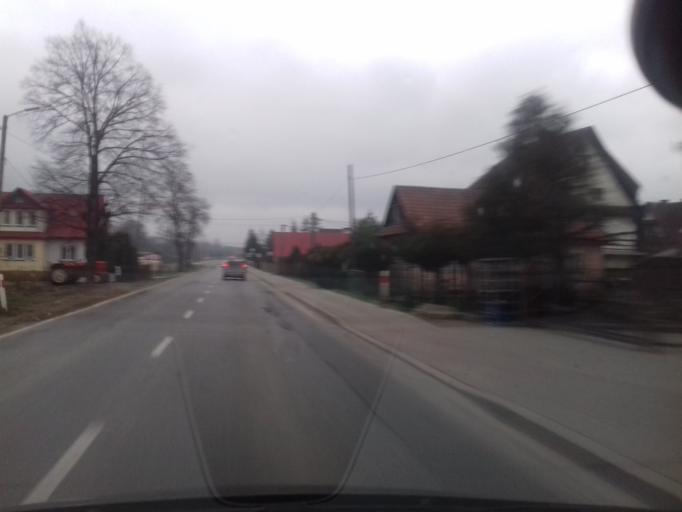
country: PL
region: Lesser Poland Voivodeship
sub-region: Powiat limanowski
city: Mszana Dolna
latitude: 49.6827
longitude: 20.0546
